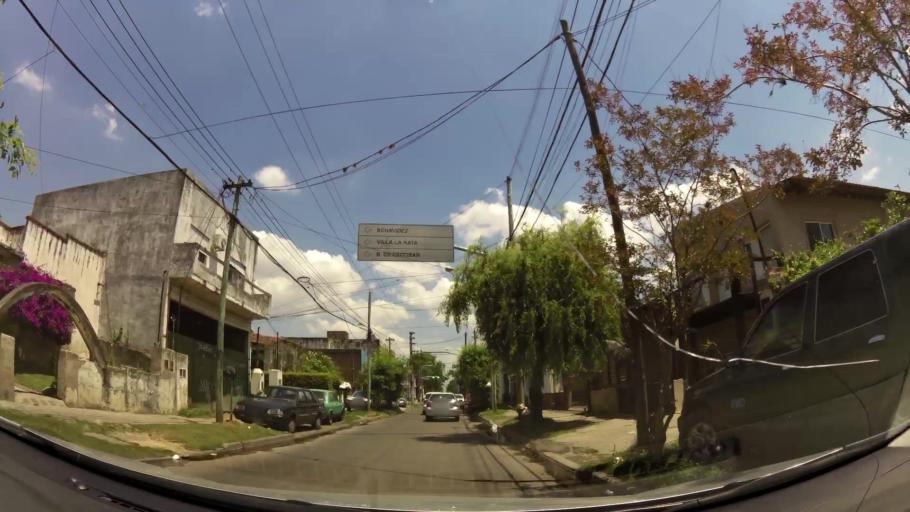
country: AR
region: Buenos Aires
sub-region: Partido de Tigre
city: Tigre
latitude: -34.4212
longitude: -58.5919
